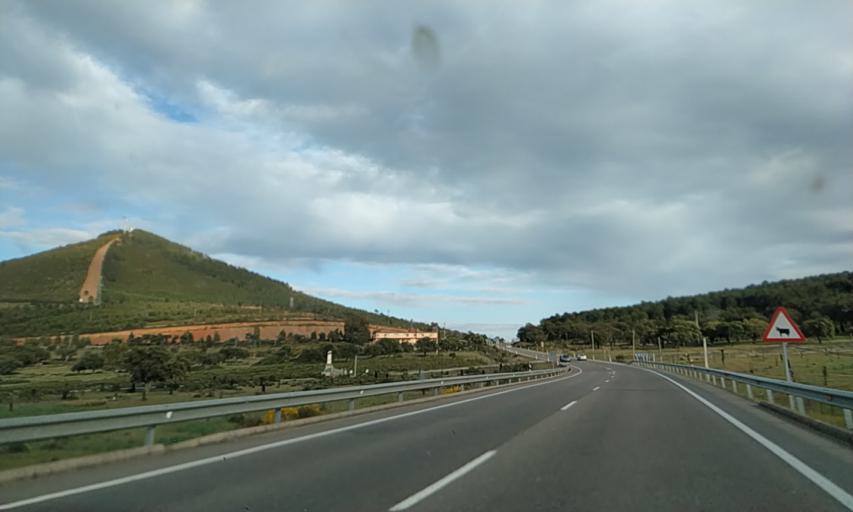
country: ES
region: Extremadura
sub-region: Provincia de Caceres
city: Canaveral
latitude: 39.8232
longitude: -6.3707
